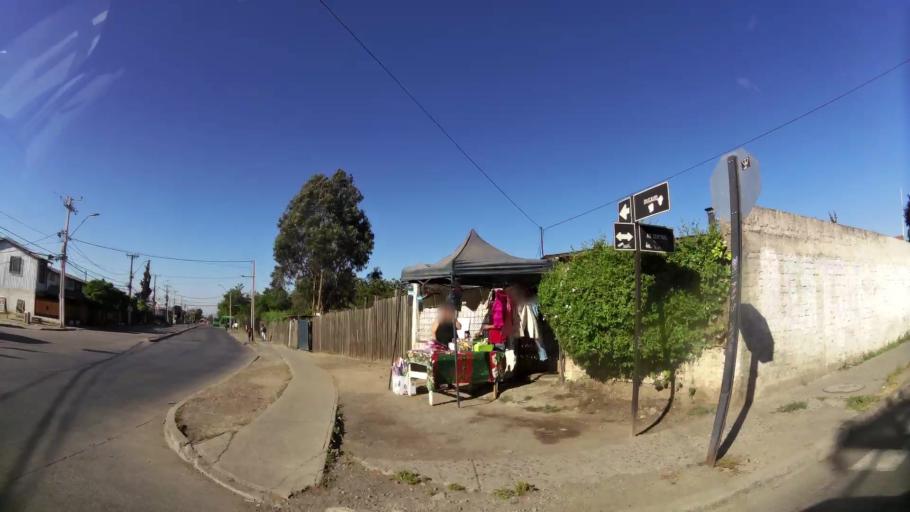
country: CL
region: Santiago Metropolitan
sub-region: Provincia de Maipo
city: San Bernardo
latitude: -33.6022
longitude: -70.6851
